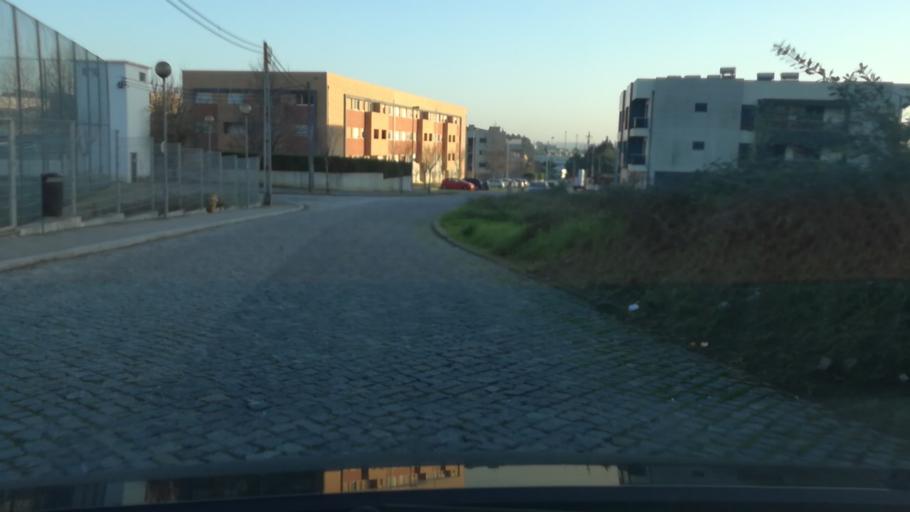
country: PT
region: Porto
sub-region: Maia
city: Anta
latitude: 41.2805
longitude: -8.6180
